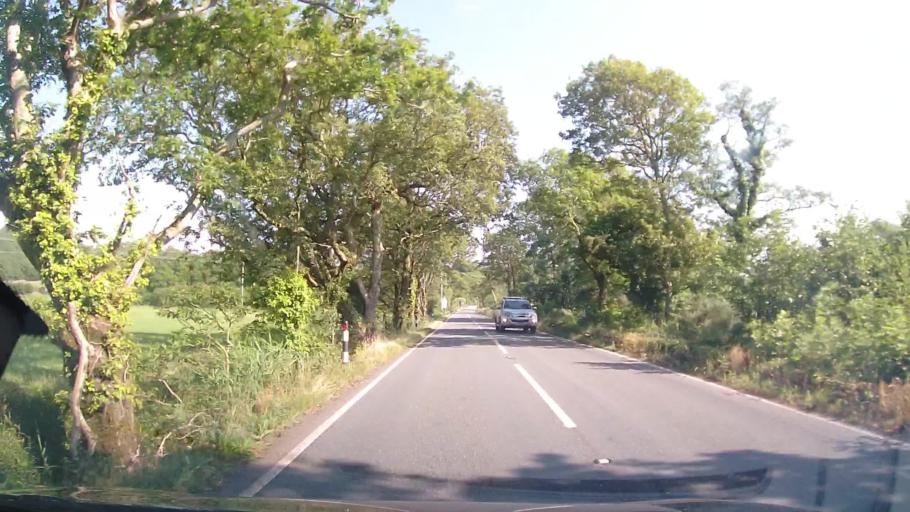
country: GB
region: Wales
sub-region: Gwynedd
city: Llanbedr
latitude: 52.8269
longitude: -4.1062
